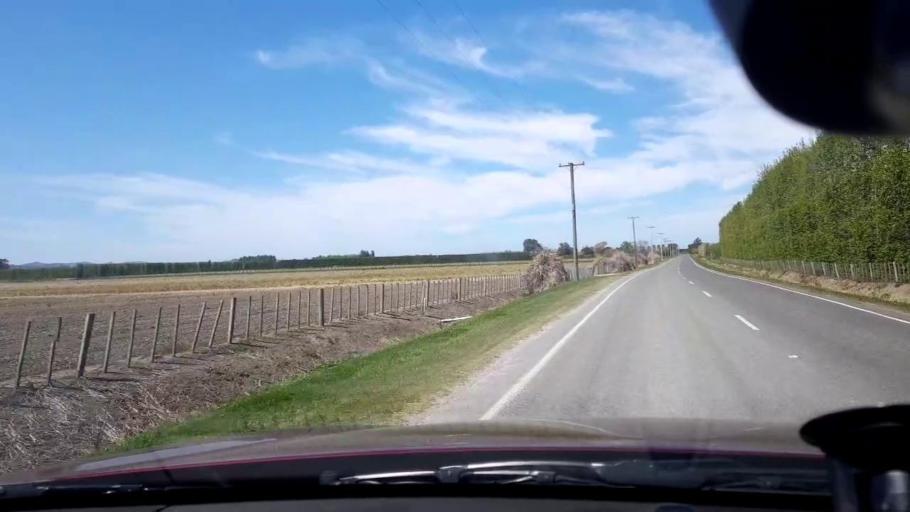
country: NZ
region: Gisborne
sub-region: Gisborne District
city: Gisborne
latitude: -38.6300
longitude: 177.9267
